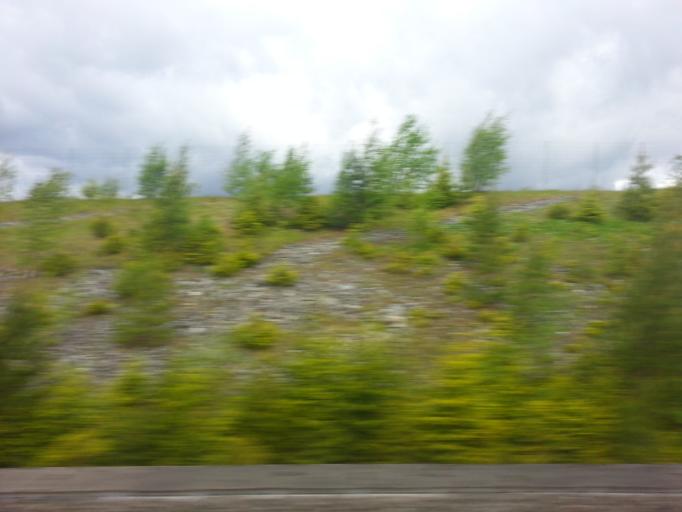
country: NO
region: Akershus
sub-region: Sorum
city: Frogner
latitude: 60.0143
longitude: 11.1108
